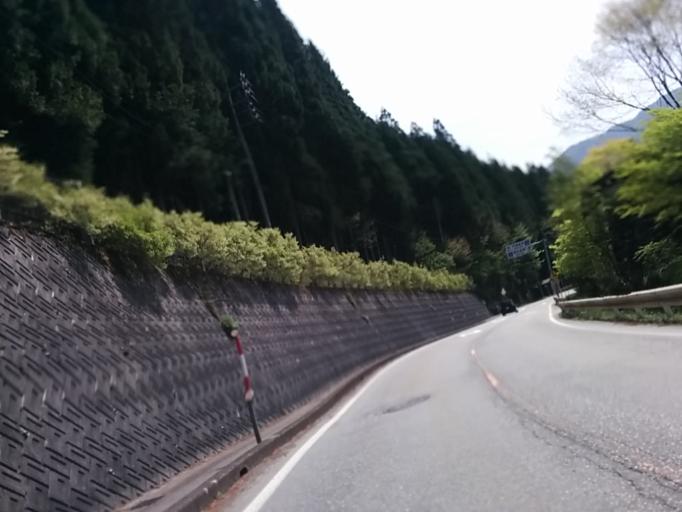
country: JP
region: Gifu
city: Takayama
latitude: 36.2328
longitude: 137.5305
